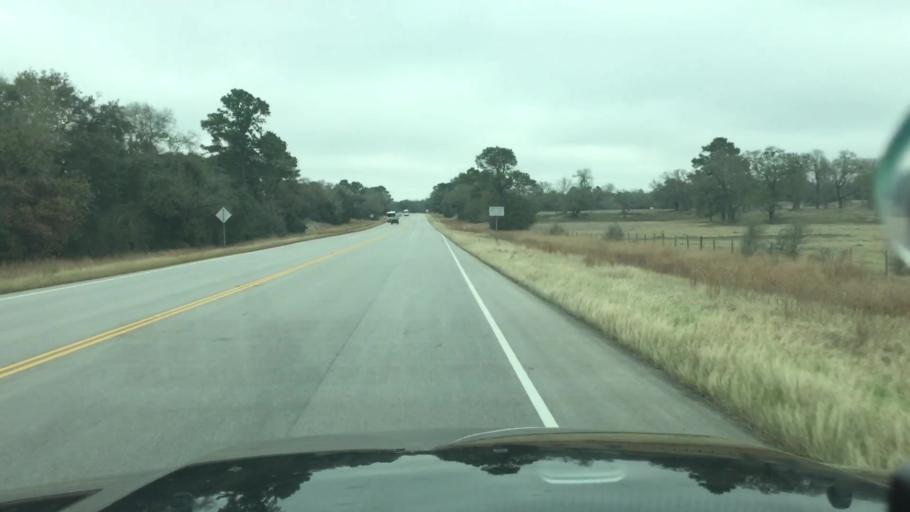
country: US
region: Texas
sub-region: Lee County
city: Giddings
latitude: 30.0869
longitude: -96.9153
